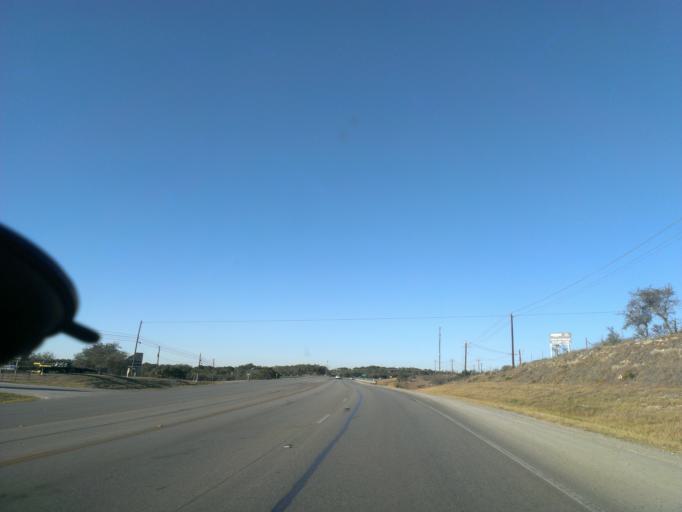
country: US
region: Texas
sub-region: Hays County
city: Dripping Springs
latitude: 30.1949
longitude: -98.0604
